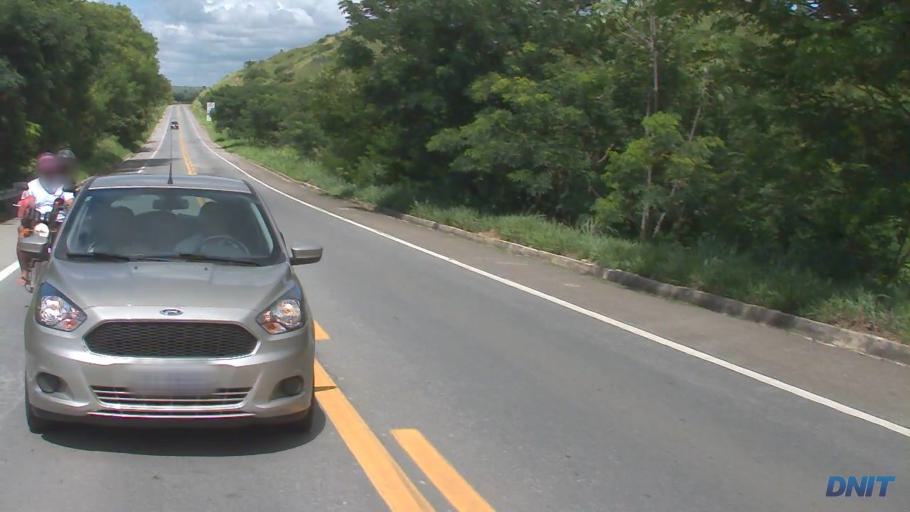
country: BR
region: Minas Gerais
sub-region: Governador Valadares
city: Governador Valadares
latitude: -18.9693
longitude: -42.0923
